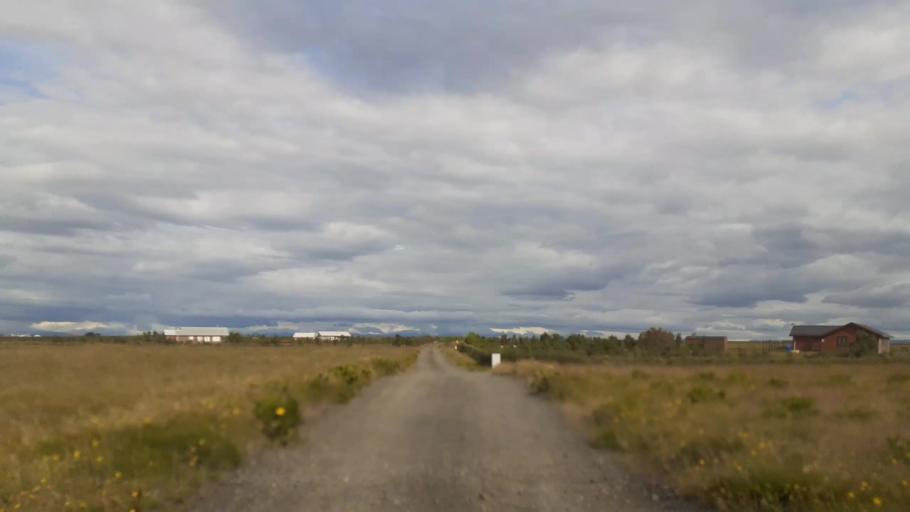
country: IS
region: South
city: Vestmannaeyjar
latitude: 63.7708
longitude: -20.2975
